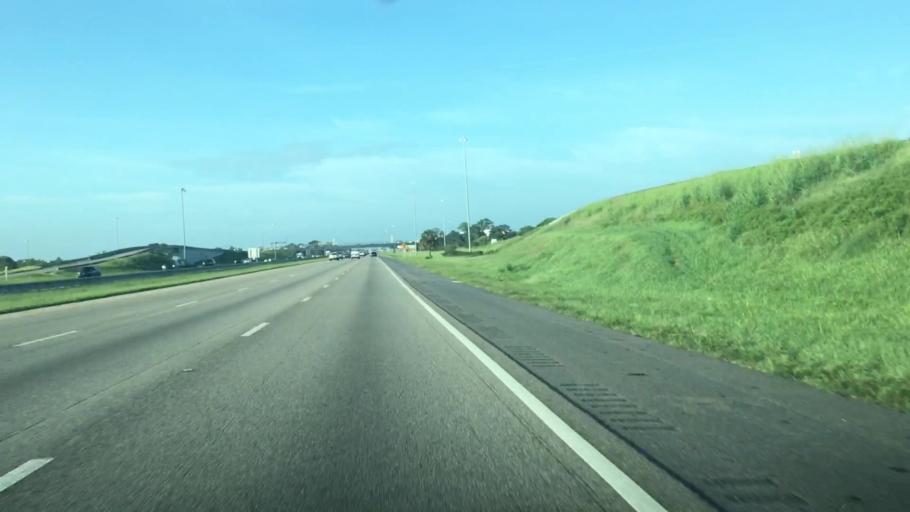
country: US
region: Florida
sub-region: Seminole County
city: Heathrow
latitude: 28.7927
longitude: -81.3487
